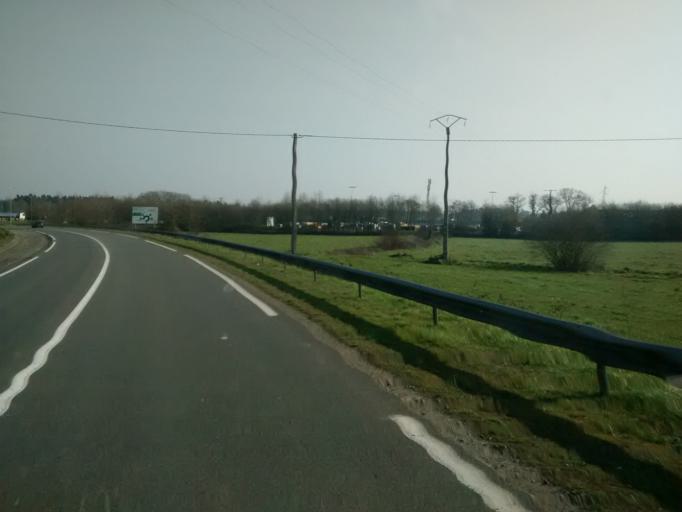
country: FR
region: Brittany
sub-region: Departement d'Ille-et-Vilaine
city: Chavagne
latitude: 48.0619
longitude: -1.7792
